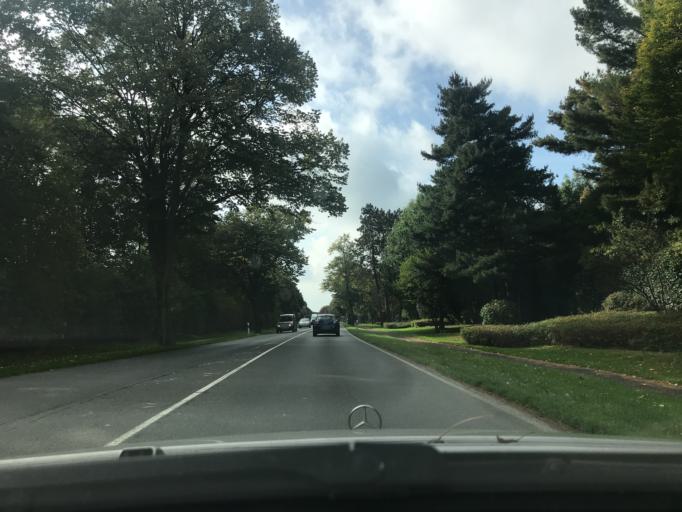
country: DE
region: North Rhine-Westphalia
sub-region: Regierungsbezirk Dusseldorf
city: Moers
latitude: 51.4460
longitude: 6.6155
